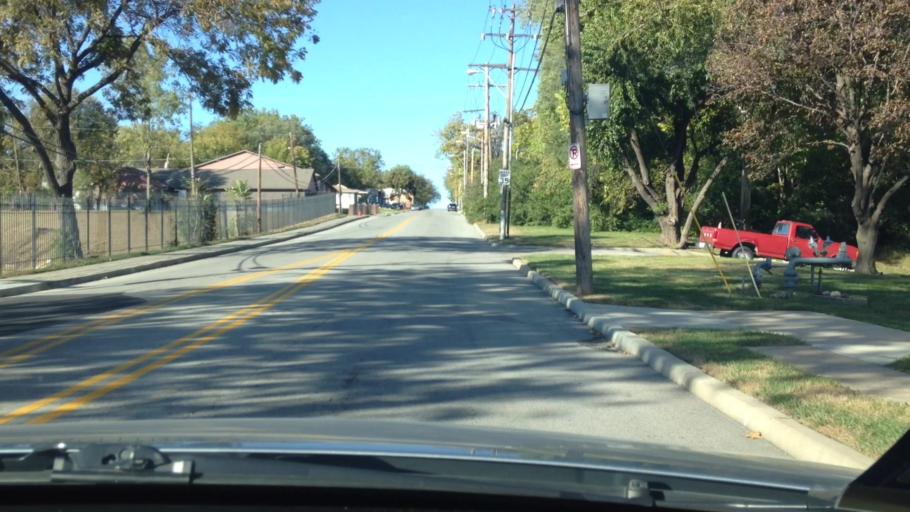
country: US
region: Kansas
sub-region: Johnson County
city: Westwood
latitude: 39.0439
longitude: -94.5635
